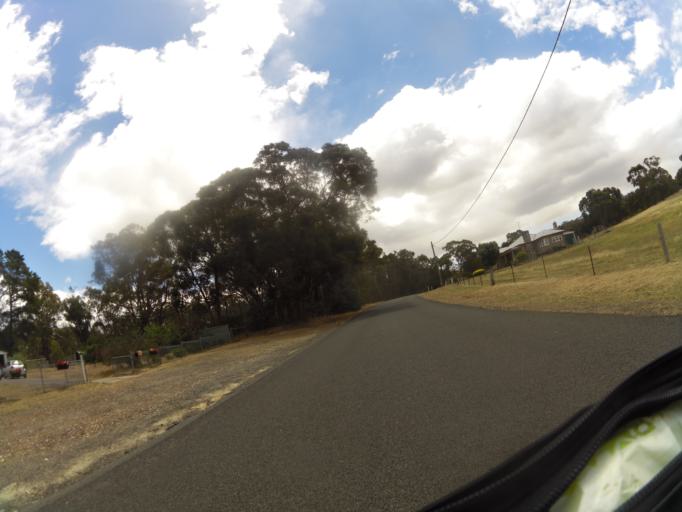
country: AU
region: Victoria
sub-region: Mount Alexander
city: Castlemaine
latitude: -37.0243
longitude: 144.2416
